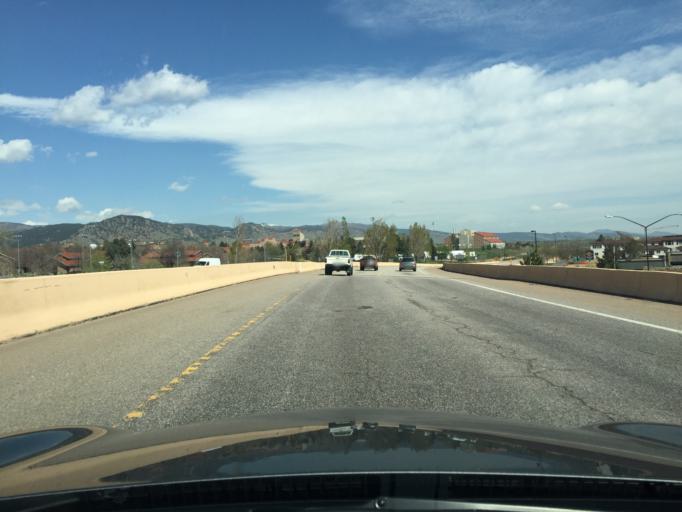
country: US
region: Colorado
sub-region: Boulder County
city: Boulder
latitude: 40.0003
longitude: -105.2579
